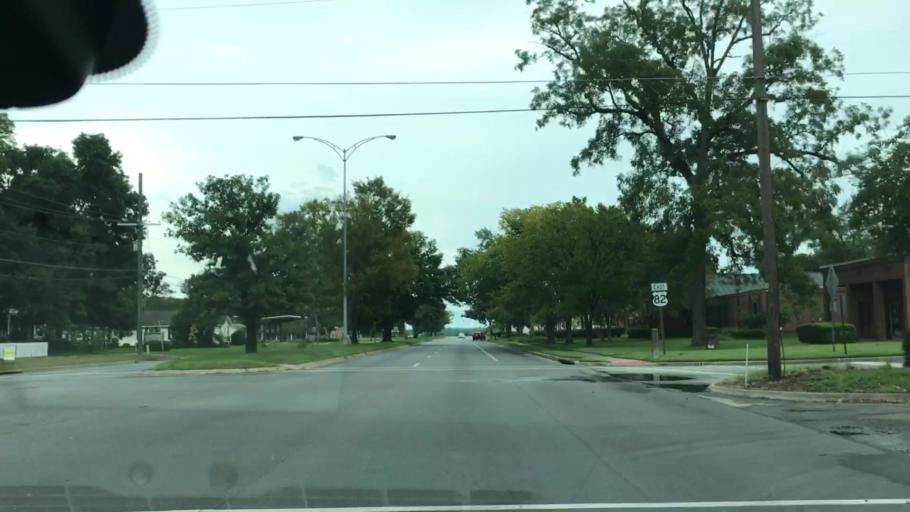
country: US
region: Alabama
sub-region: Barbour County
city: Eufaula
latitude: 31.8914
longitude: -85.1391
